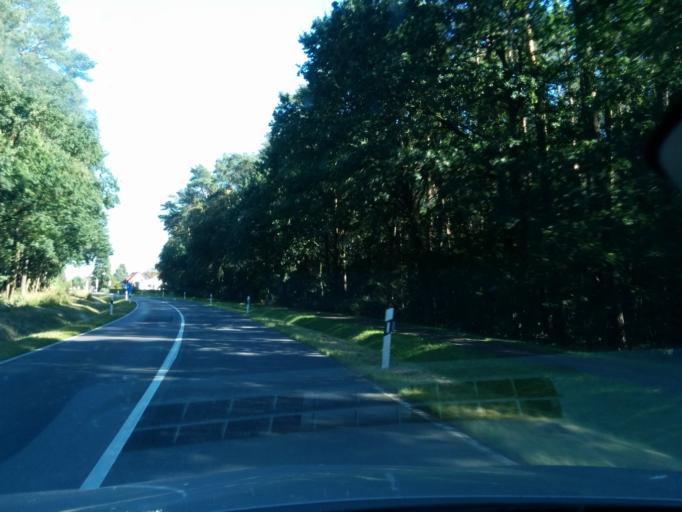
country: DE
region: Mecklenburg-Vorpommern
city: Torgelow
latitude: 53.6324
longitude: 13.9900
